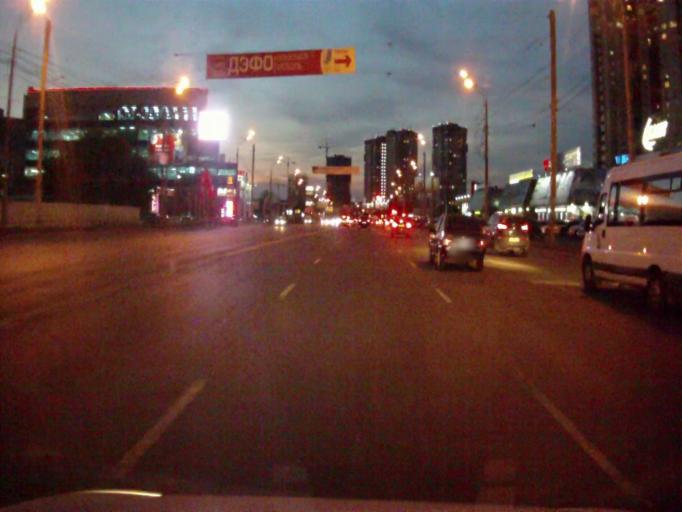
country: RU
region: Chelyabinsk
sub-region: Gorod Chelyabinsk
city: Chelyabinsk
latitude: 55.1684
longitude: 61.3782
